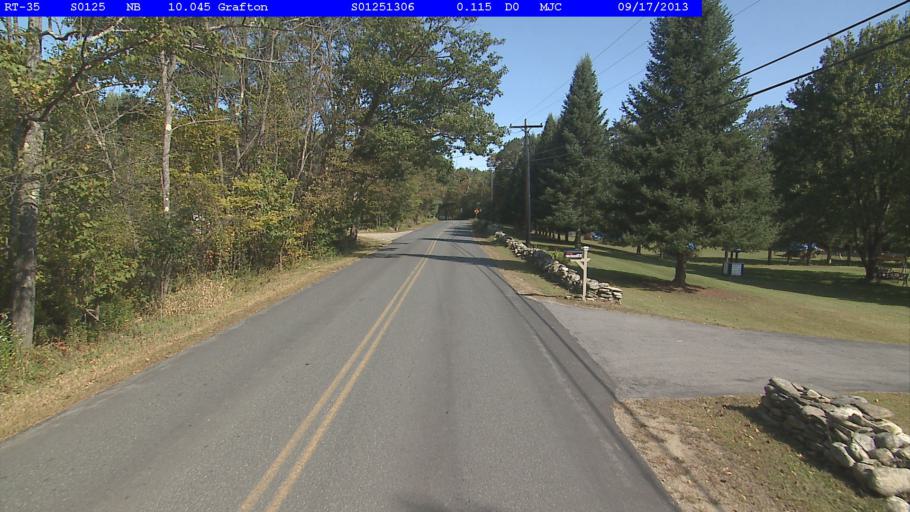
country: US
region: Vermont
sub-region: Windham County
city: Rockingham
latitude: 43.1487
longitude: -72.5614
